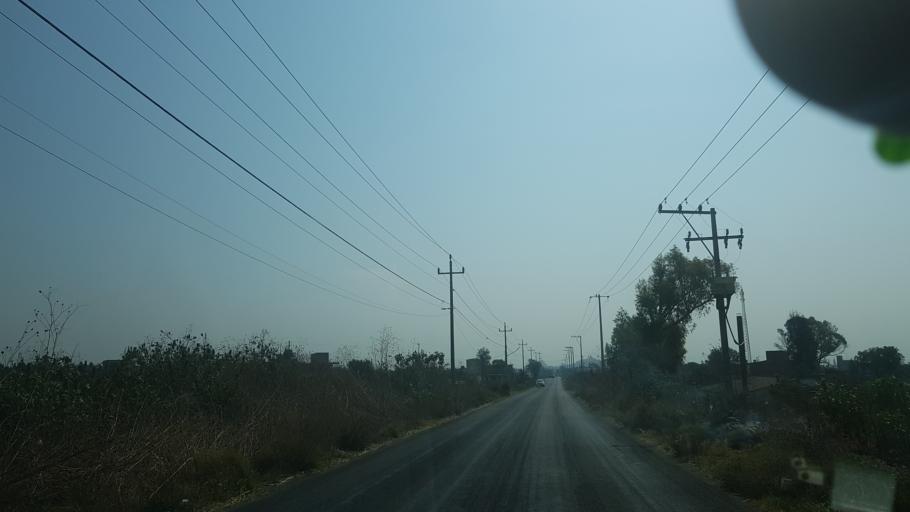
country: MX
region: Puebla
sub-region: San Jeronimo Tecuanipan
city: Los Reyes Tlanechicolpan
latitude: 19.0545
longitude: -98.3353
